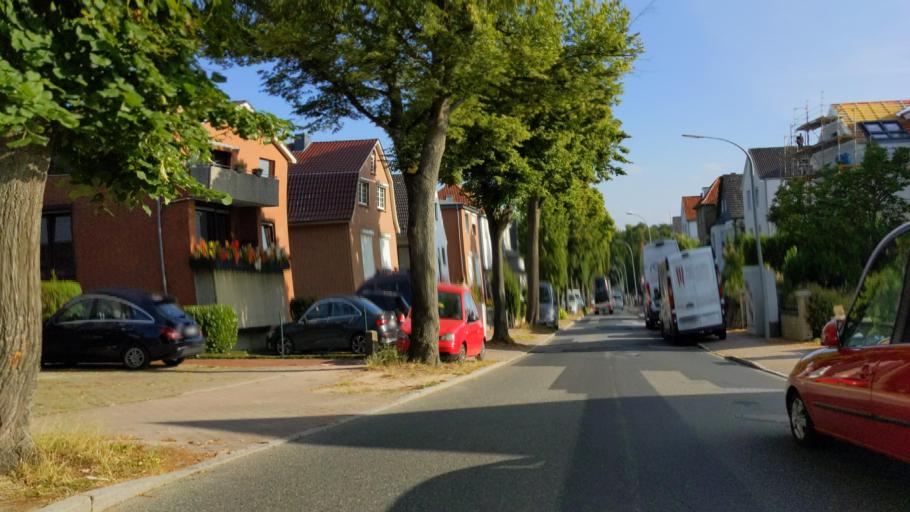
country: DE
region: Schleswig-Holstein
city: Bad Schwartau
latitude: 53.9298
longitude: 10.6916
